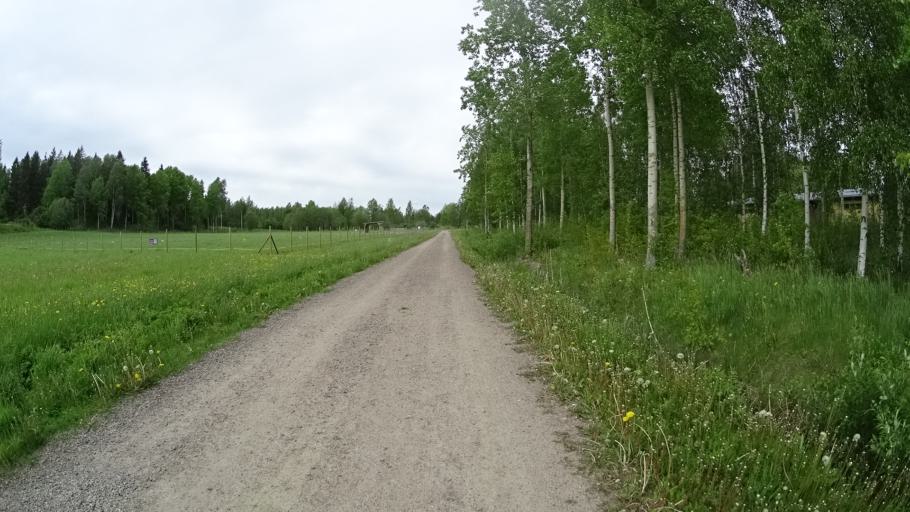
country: FI
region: Uusimaa
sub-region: Helsinki
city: Vantaa
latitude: 60.3025
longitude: 25.0126
